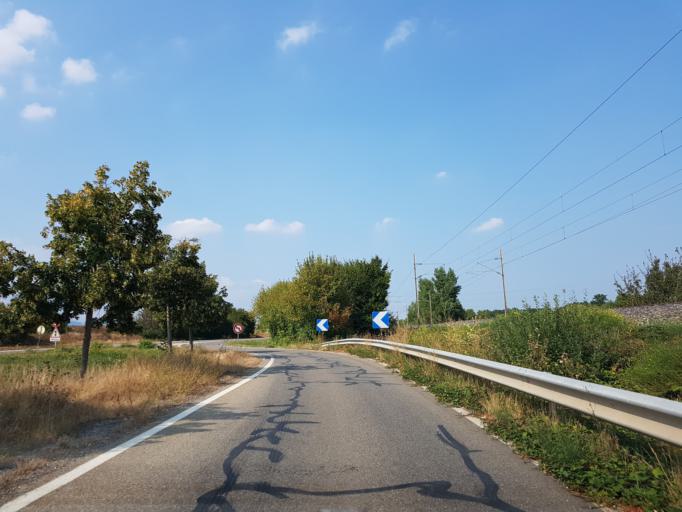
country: FR
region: Alsace
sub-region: Departement du Haut-Rhin
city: Eguisheim
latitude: 48.0440
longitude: 7.3245
